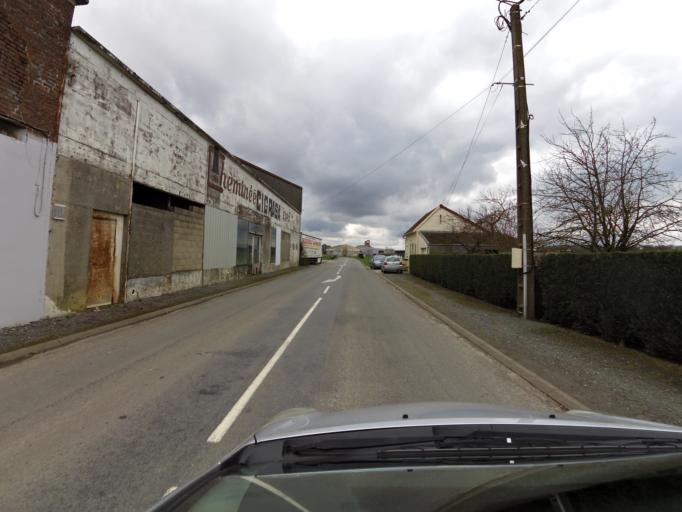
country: FR
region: Picardie
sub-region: Departement de la Somme
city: Chaulnes
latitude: 49.8748
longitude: 2.8145
